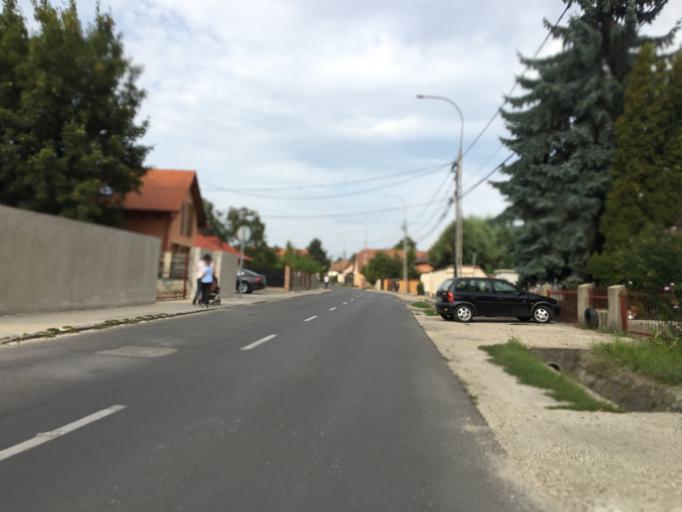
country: HU
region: Pest
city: Szigetszentmiklos
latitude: 47.3392
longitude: 19.0432
